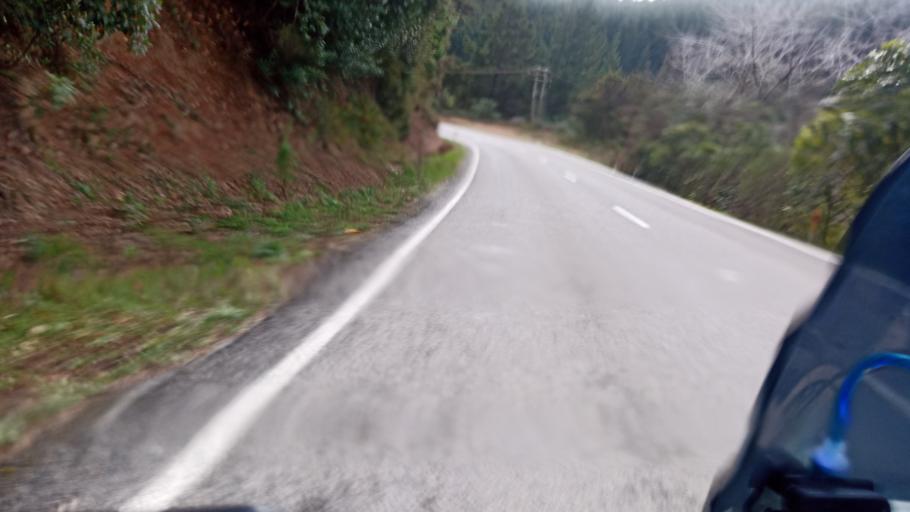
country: NZ
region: Gisborne
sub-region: Gisborne District
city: Gisborne
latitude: -37.9876
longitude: 178.2764
